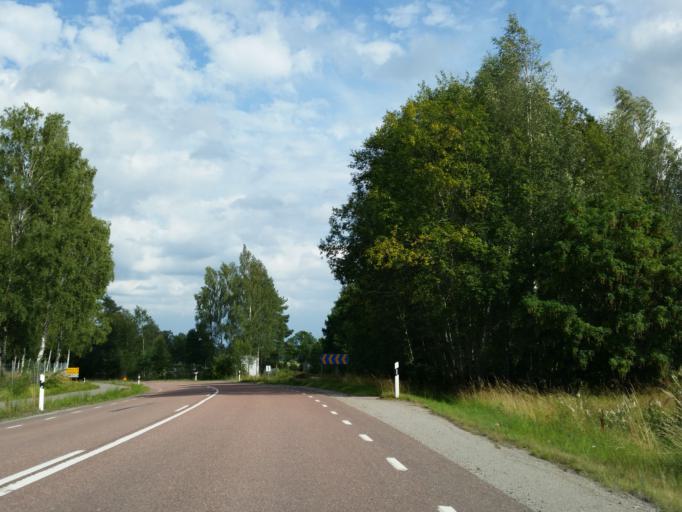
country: SE
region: Soedermanland
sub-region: Strangnas Kommun
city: Mariefred
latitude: 59.2187
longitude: 17.2889
